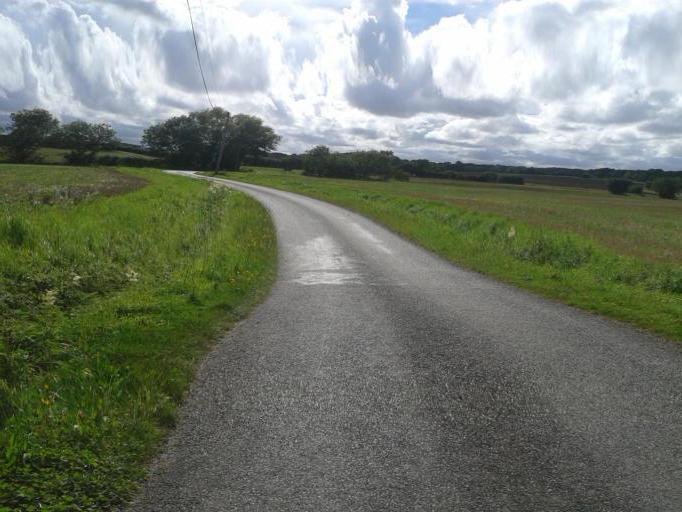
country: GB
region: England
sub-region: Hertfordshire
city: Reed
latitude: 51.9837
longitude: 0.0902
